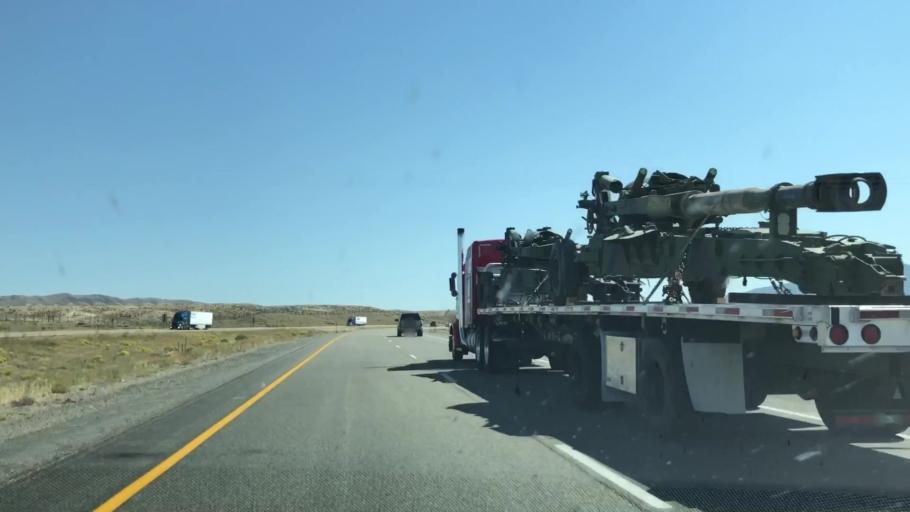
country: US
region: Wyoming
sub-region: Carbon County
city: Saratoga
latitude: 41.7414
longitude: -106.7749
